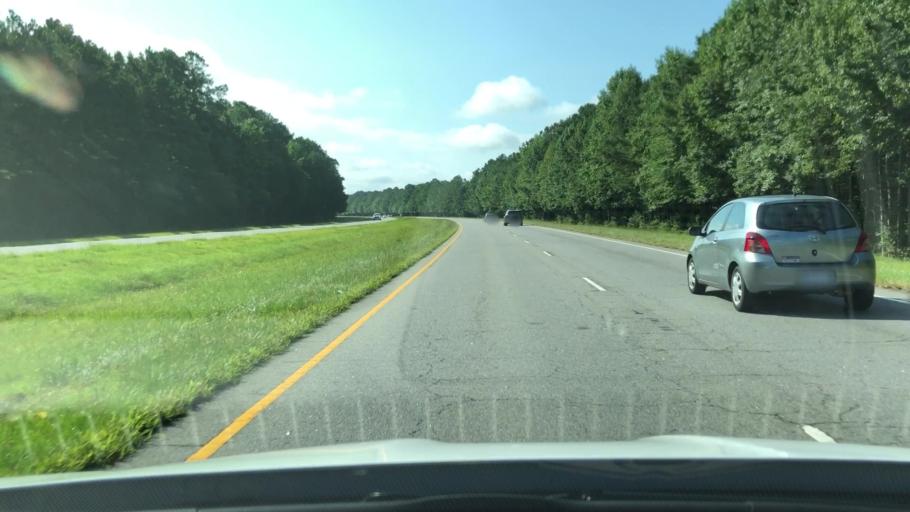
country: US
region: North Carolina
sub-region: Pasquotank County
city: Elizabeth City
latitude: 36.4084
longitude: -76.3389
